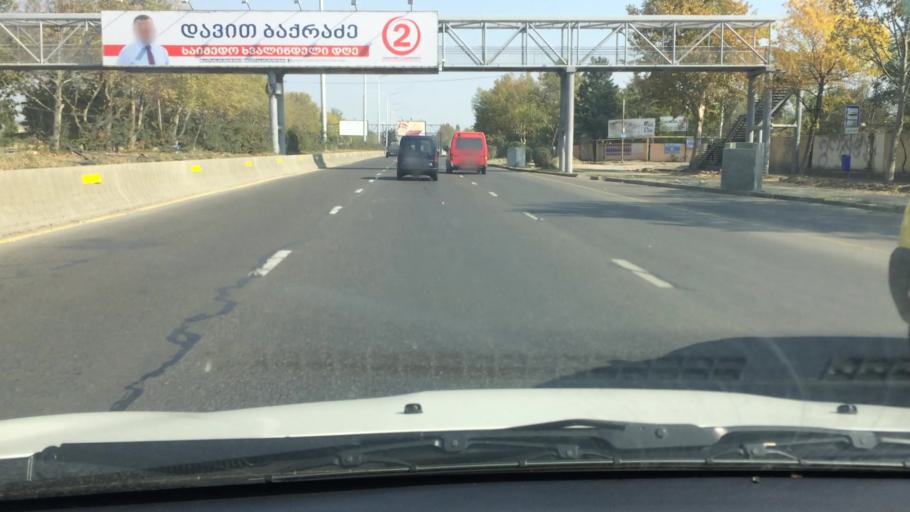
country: GE
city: Didi Lilo
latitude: 41.6896
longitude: 44.9333
